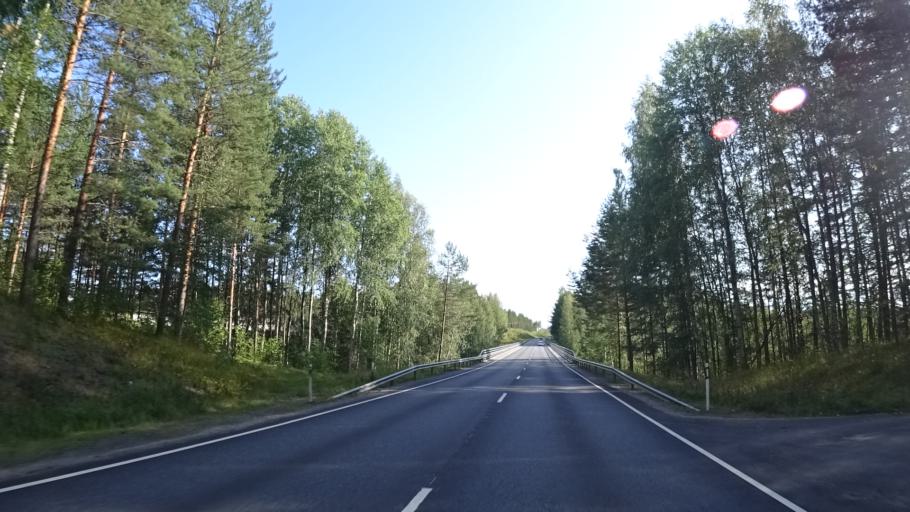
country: FI
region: North Karelia
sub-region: Keski-Karjala
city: Kesaelahti
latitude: 62.0352
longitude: 29.8980
